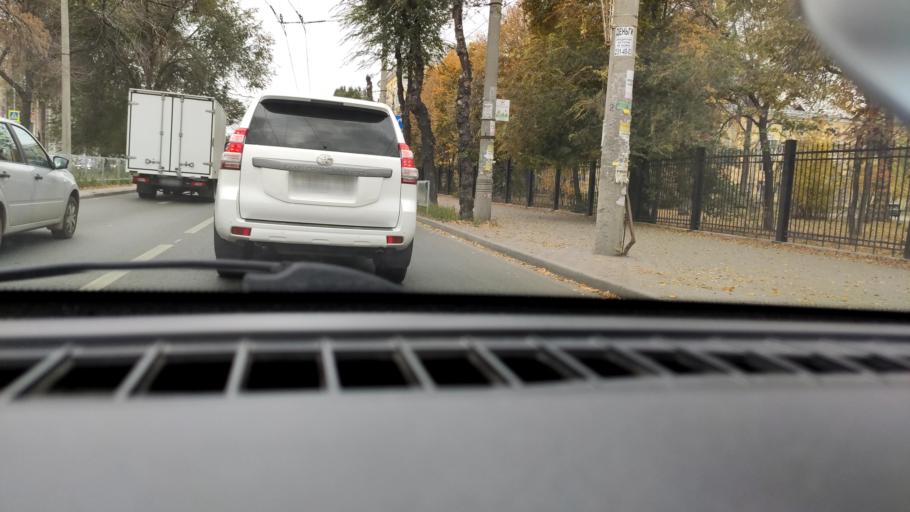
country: RU
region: Samara
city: Samara
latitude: 53.2159
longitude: 50.2549
